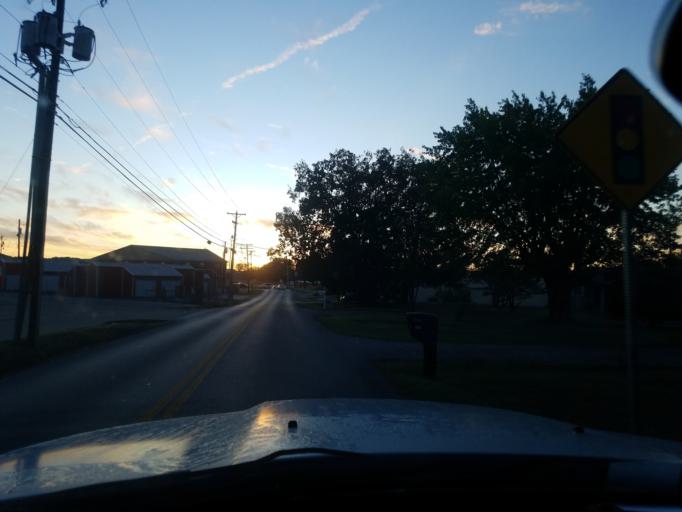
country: US
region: Kentucky
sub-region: Laurel County
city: London
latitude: 37.0948
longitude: -84.0680
